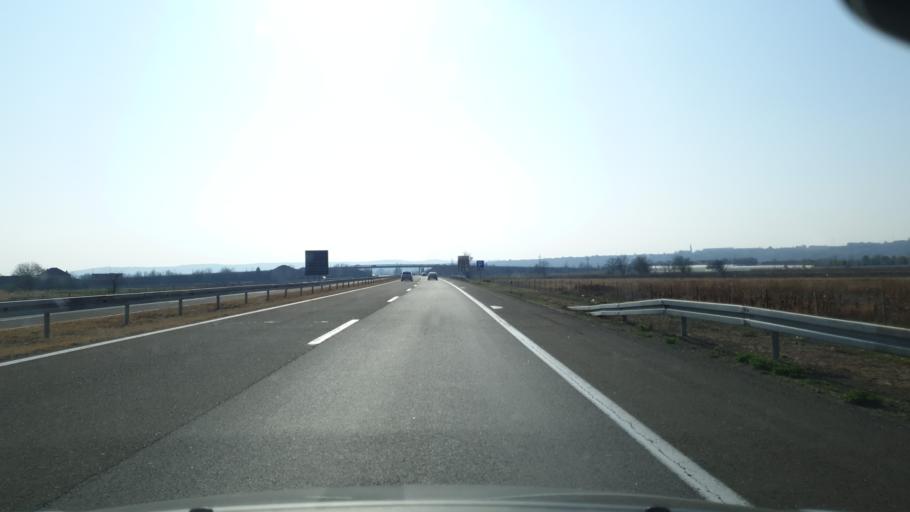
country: RS
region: Central Serbia
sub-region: Nisavski Okrug
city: Merosina
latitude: 43.3188
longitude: 21.8047
